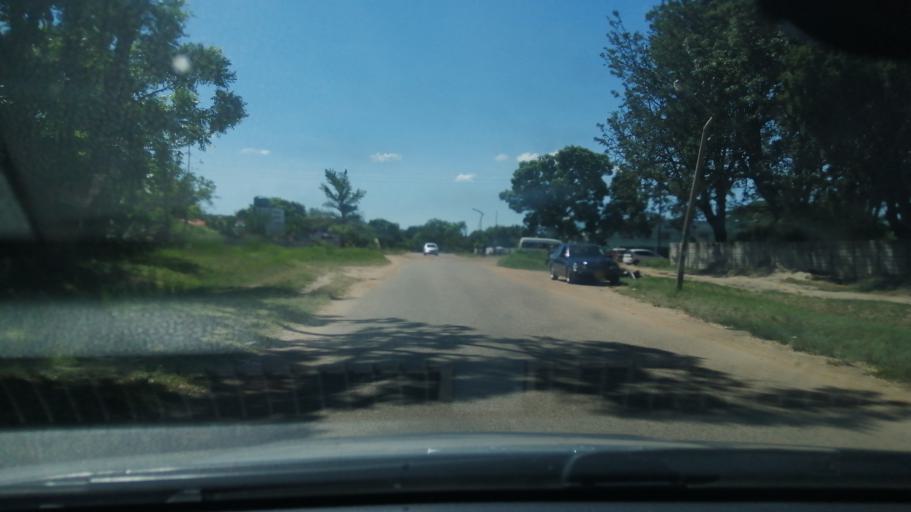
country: ZW
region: Harare
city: Epworth
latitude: -17.8190
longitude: 31.1301
